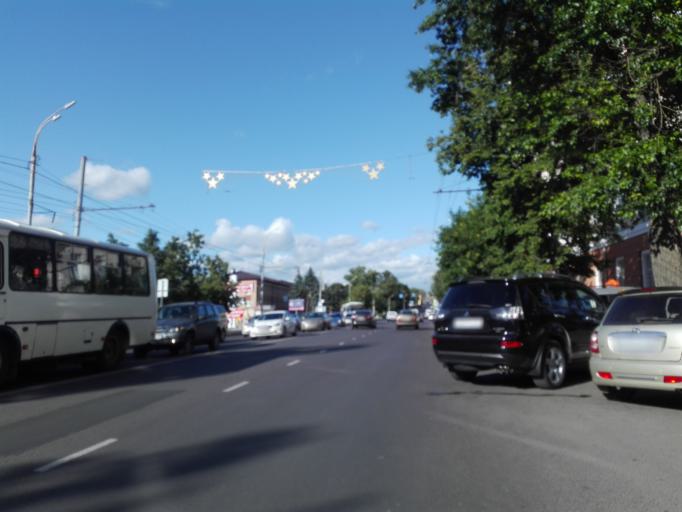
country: RU
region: Orjol
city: Orel
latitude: 52.9731
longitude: 36.0899
